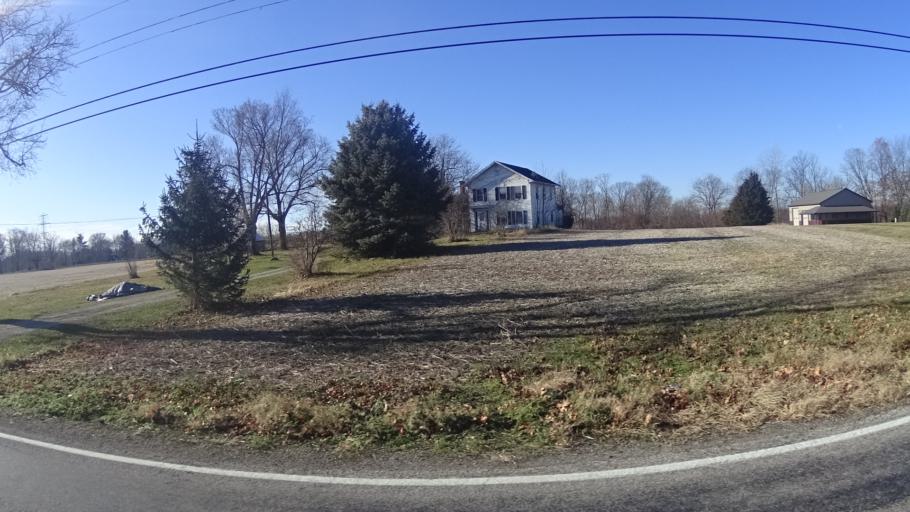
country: US
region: Ohio
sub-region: Lorain County
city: Vermilion-on-the-Lake
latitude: 41.3785
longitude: -82.3101
